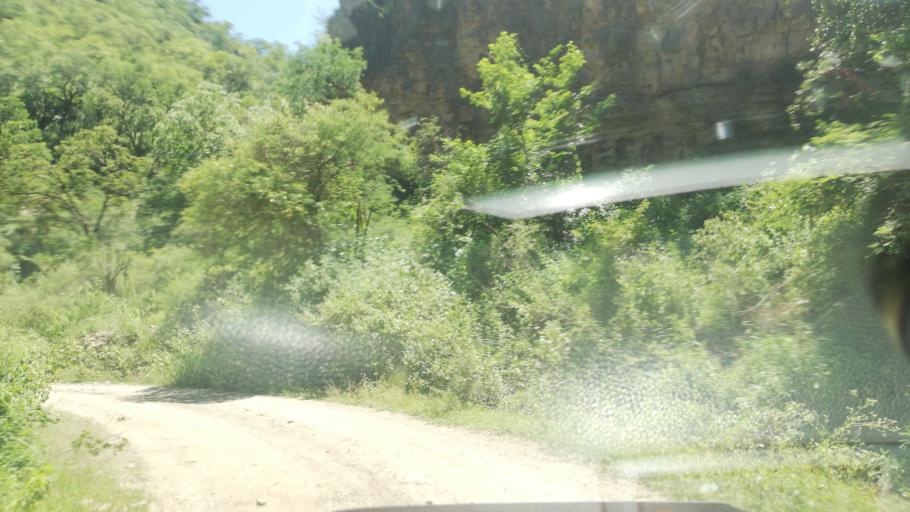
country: BO
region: Cochabamba
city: Mizque
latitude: -17.8297
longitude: -65.3042
